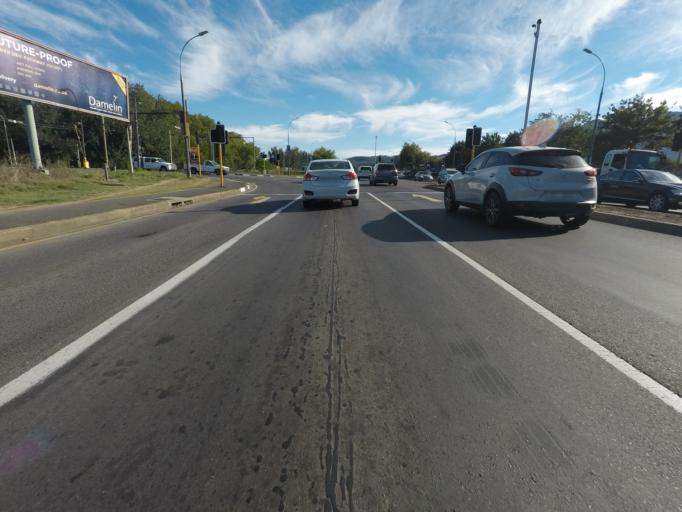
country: ZA
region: Western Cape
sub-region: Cape Winelands District Municipality
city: Stellenbosch
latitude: -33.9347
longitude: 18.8523
